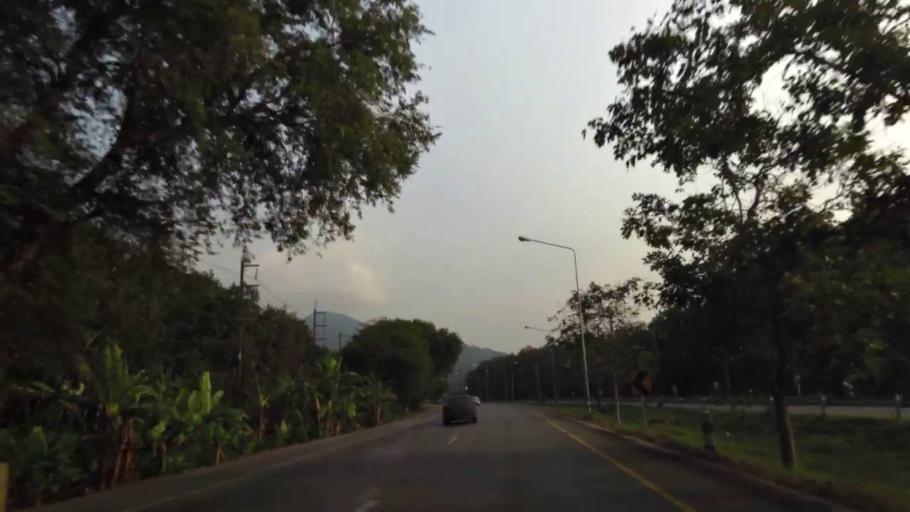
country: TH
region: Chanthaburi
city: Chanthaburi
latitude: 12.5774
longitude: 102.1601
